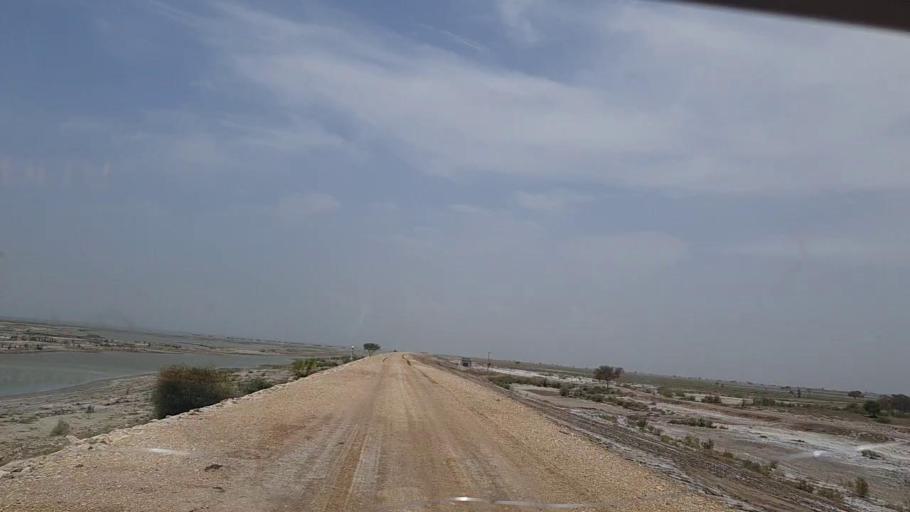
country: PK
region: Sindh
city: Sehwan
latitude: 26.4157
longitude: 67.7573
